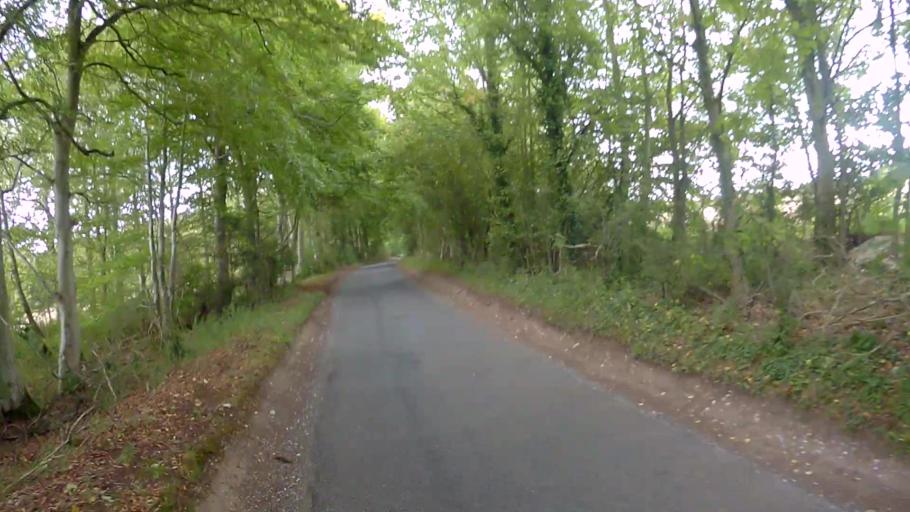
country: GB
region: England
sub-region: Hampshire
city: Overton
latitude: 51.1907
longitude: -1.2782
